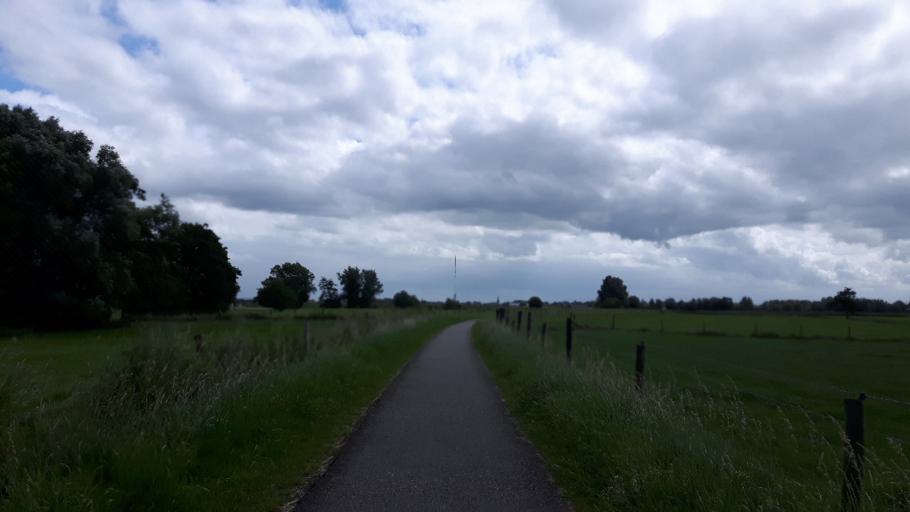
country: NL
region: Utrecht
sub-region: Gemeente IJsselstein
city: IJsselstein
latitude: 52.0486
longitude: 5.0127
